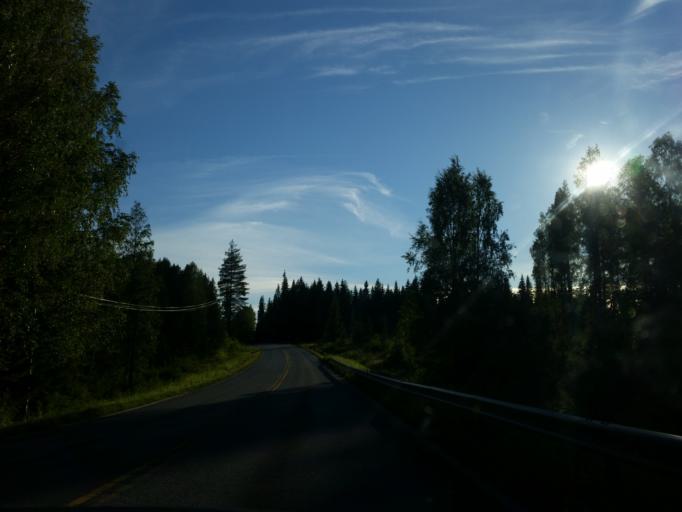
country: FI
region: Northern Savo
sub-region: Kuopio
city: Kuopio
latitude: 62.8461
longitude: 27.4556
